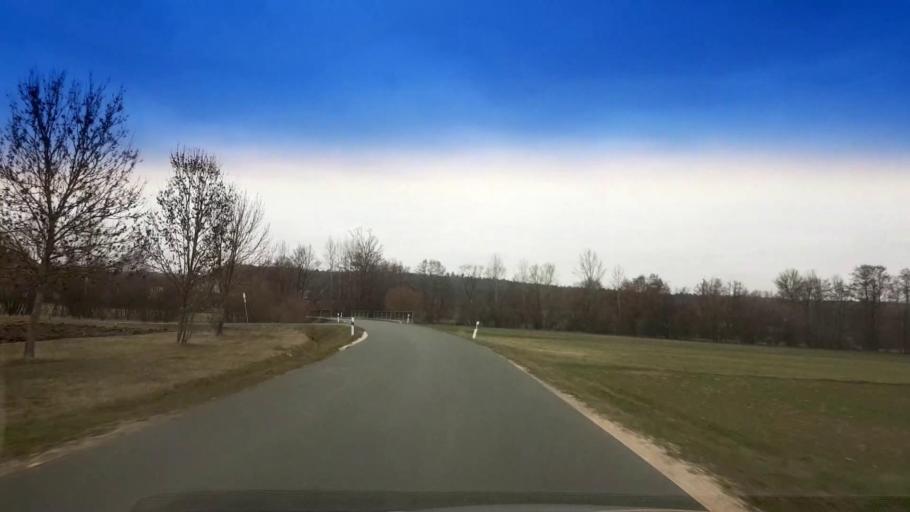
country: DE
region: Bavaria
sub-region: Upper Franconia
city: Pettstadt
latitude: 49.7932
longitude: 10.9055
